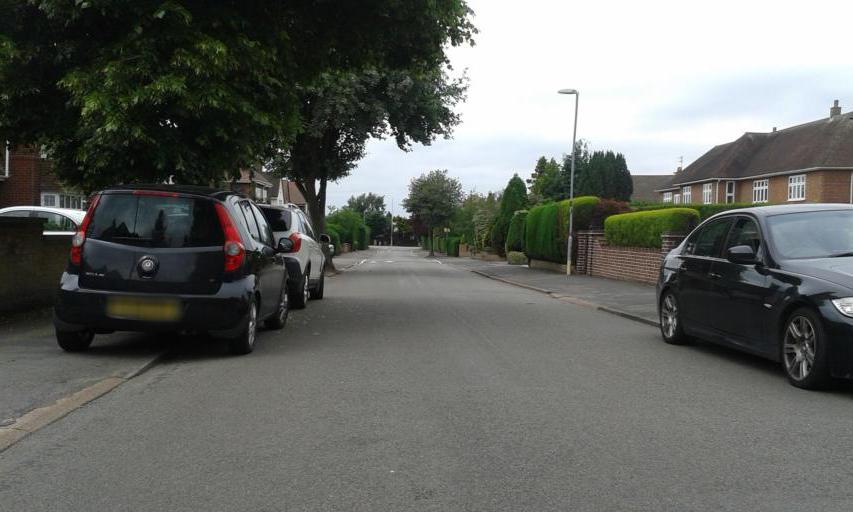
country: GB
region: England
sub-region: Leicestershire
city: Hinckley
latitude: 52.5490
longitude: -1.3547
